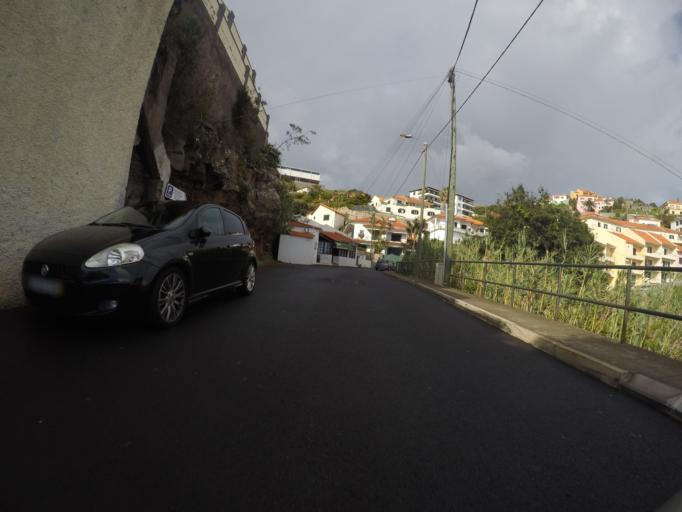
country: PT
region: Madeira
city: Canico
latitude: 32.6472
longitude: -16.8557
